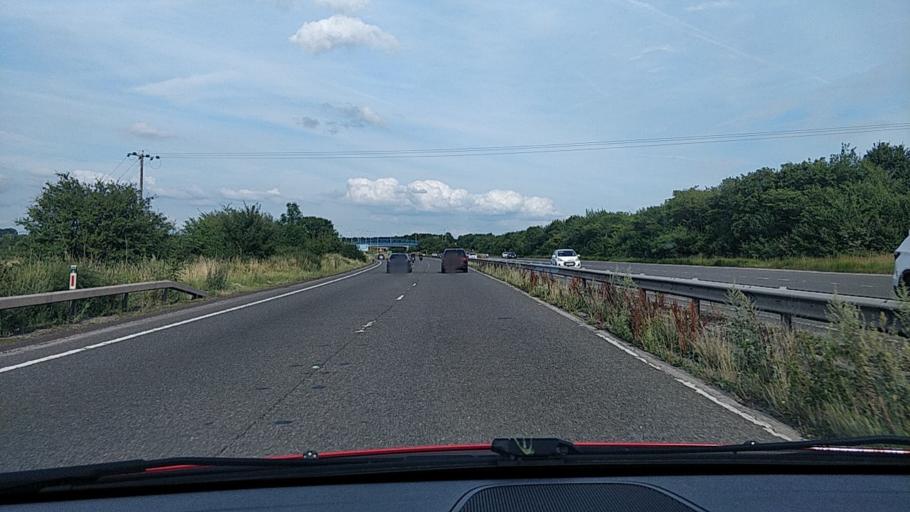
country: GB
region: England
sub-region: Cheshire West and Chester
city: Eccleston
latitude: 53.1561
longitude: -2.9219
